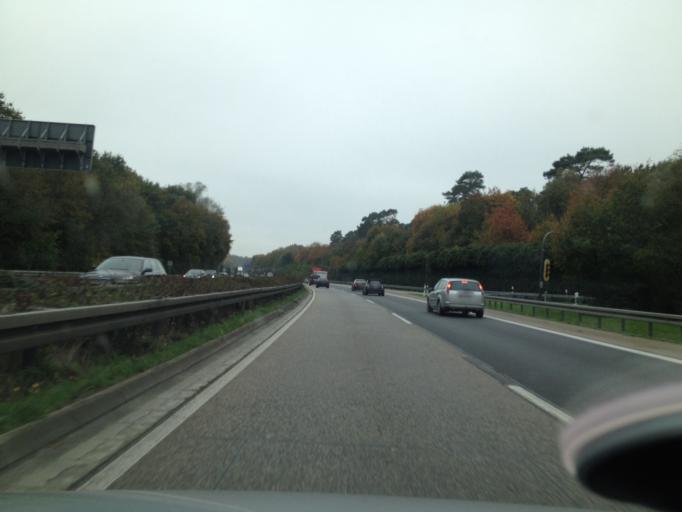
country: DE
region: North Rhine-Westphalia
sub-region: Regierungsbezirk Koln
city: Bergisch Gladbach
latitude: 50.9499
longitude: 7.1264
